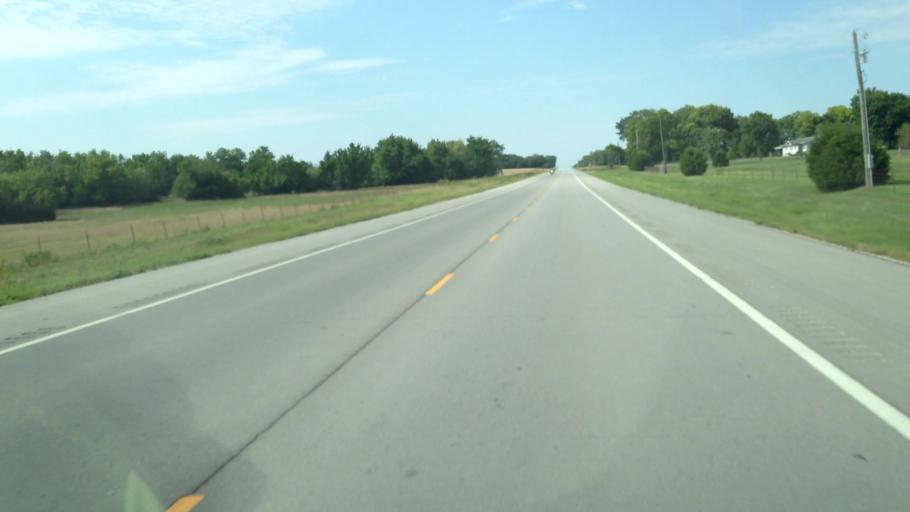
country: US
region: Kansas
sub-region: Labette County
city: Parsons
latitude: 37.2967
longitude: -95.2675
